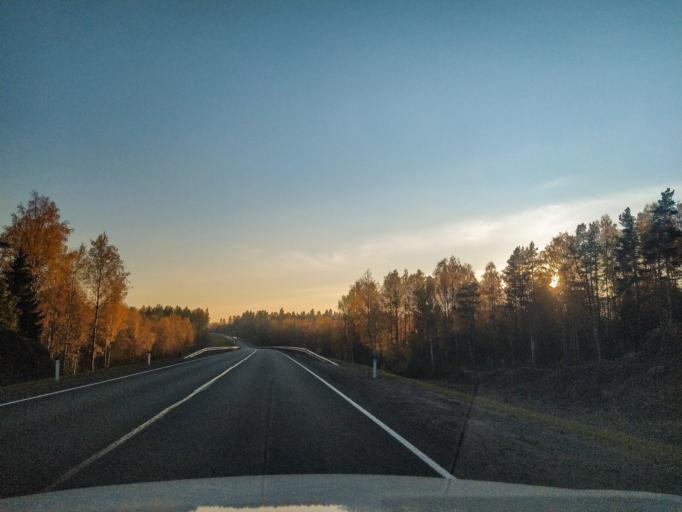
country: RU
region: Leningrad
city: Kuznechnoye
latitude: 61.3657
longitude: 29.9002
